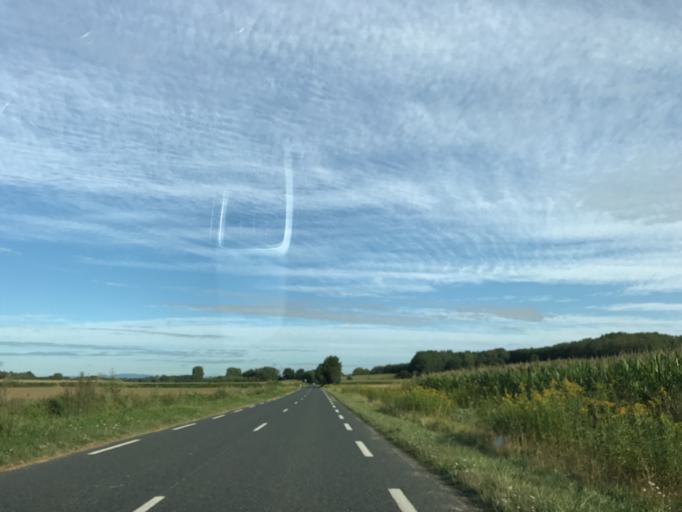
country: FR
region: Rhone-Alpes
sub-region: Departement de l'Ain
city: Miribel
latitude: 45.8411
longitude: 4.9417
